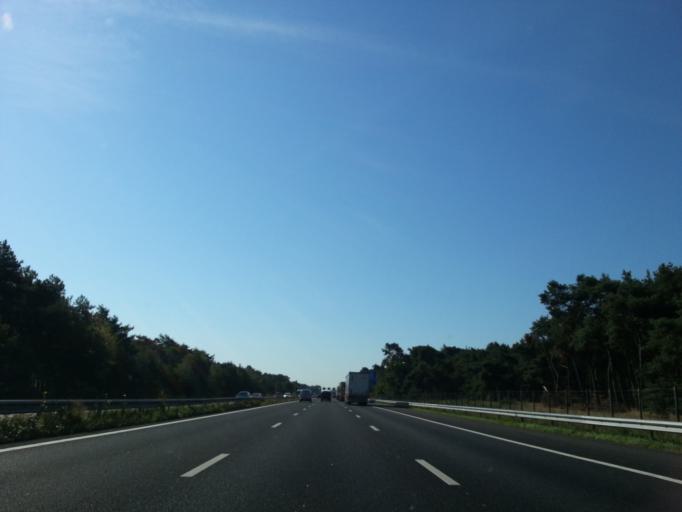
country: NL
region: North Brabant
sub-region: Gemeente Heeze-Leende
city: Heeze
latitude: 51.3629
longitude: 5.5304
